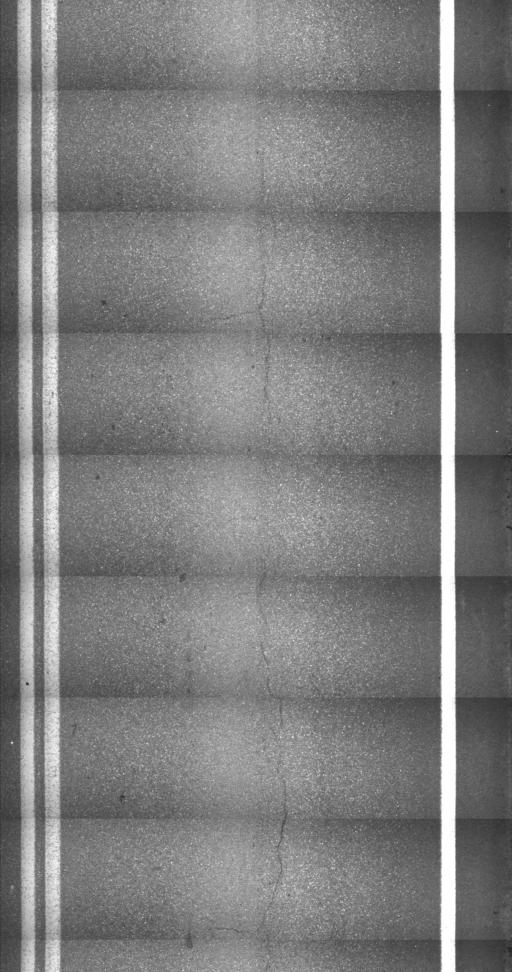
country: US
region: New York
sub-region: Clinton County
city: Cumberland Head
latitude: 44.6662
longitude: -73.3292
